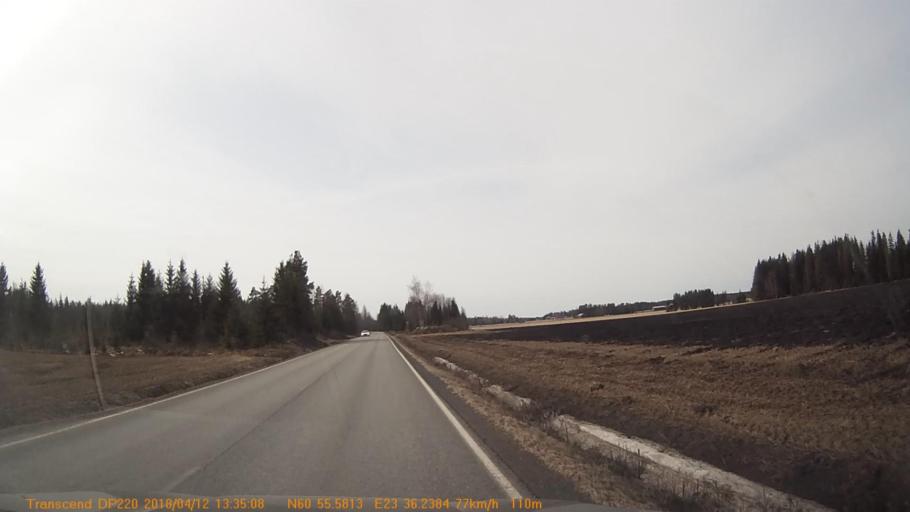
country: FI
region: Haeme
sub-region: Forssa
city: Forssa
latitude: 60.9263
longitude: 23.6036
